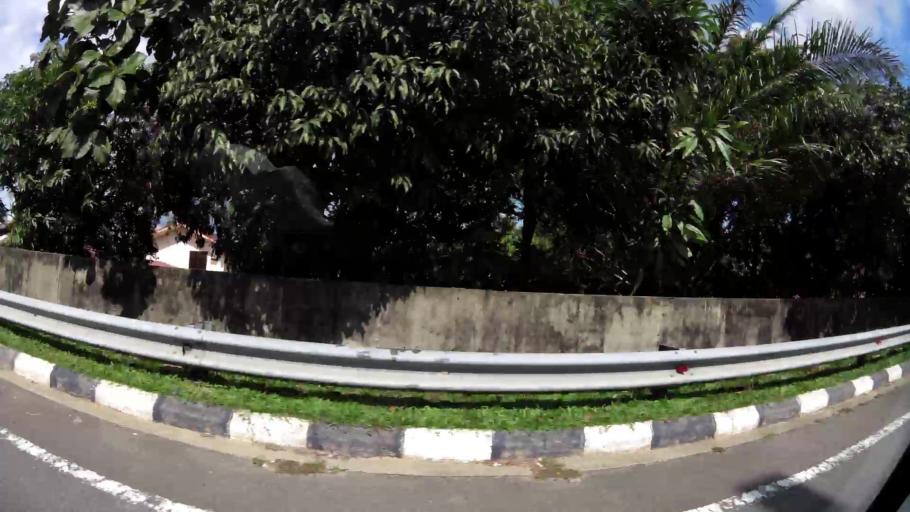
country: BN
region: Brunei and Muara
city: Bandar Seri Begawan
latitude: 4.9616
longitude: 114.9519
